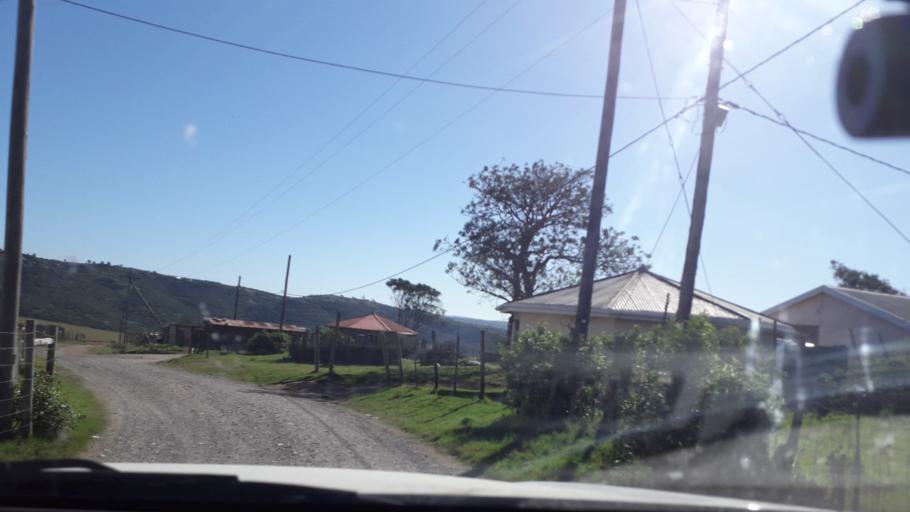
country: ZA
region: Eastern Cape
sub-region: Buffalo City Metropolitan Municipality
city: East London
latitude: -32.8439
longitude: 27.9871
